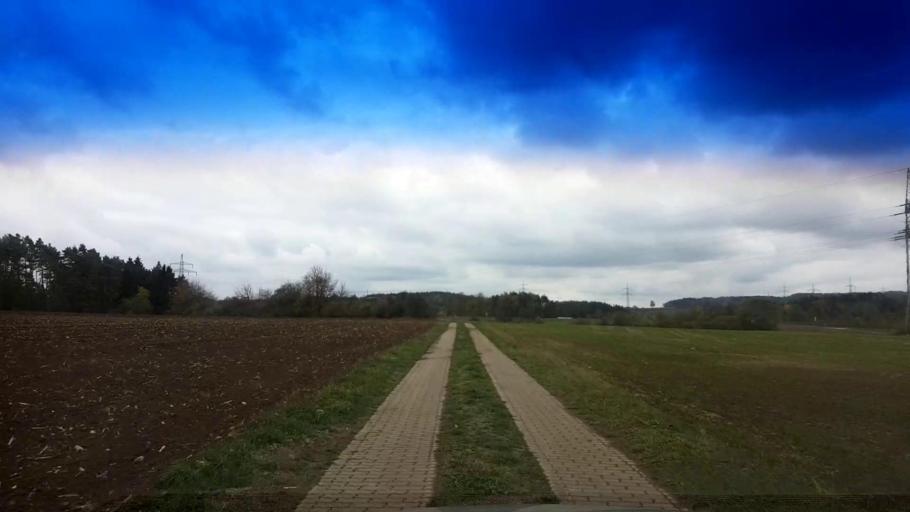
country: DE
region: Bavaria
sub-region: Upper Franconia
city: Poxdorf
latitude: 49.9794
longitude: 11.1186
